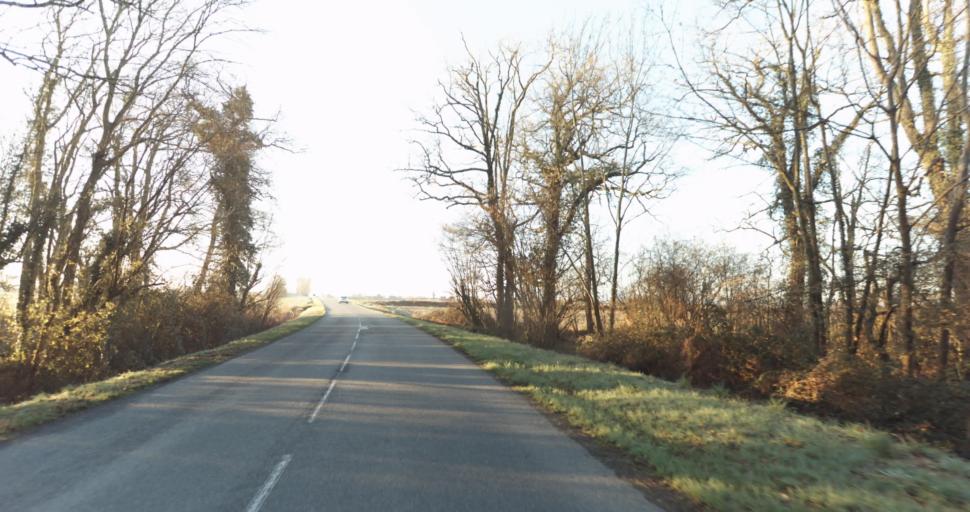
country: FR
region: Aquitaine
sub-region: Departement des Pyrenees-Atlantiques
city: Morlaas
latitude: 43.3206
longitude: -0.2748
